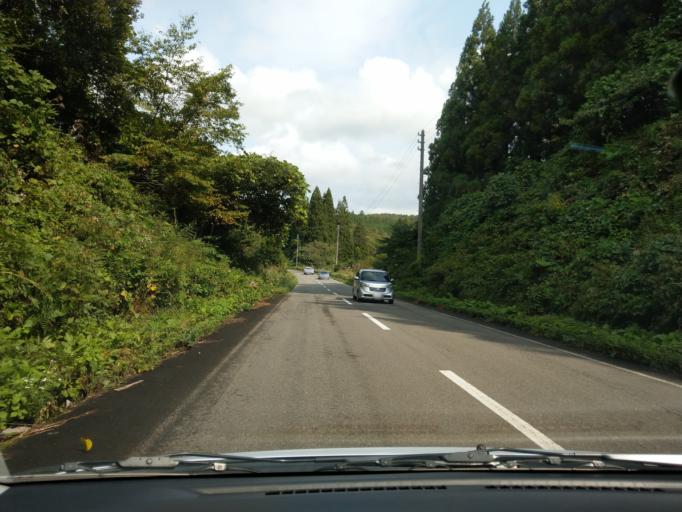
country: JP
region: Akita
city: Omagari
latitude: 39.4787
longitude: 140.3108
